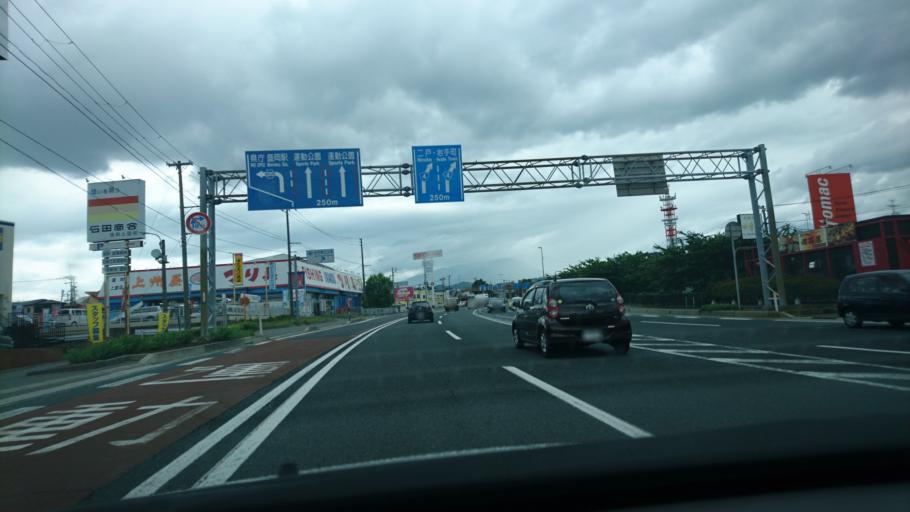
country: JP
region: Iwate
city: Morioka-shi
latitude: 39.7257
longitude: 141.1245
